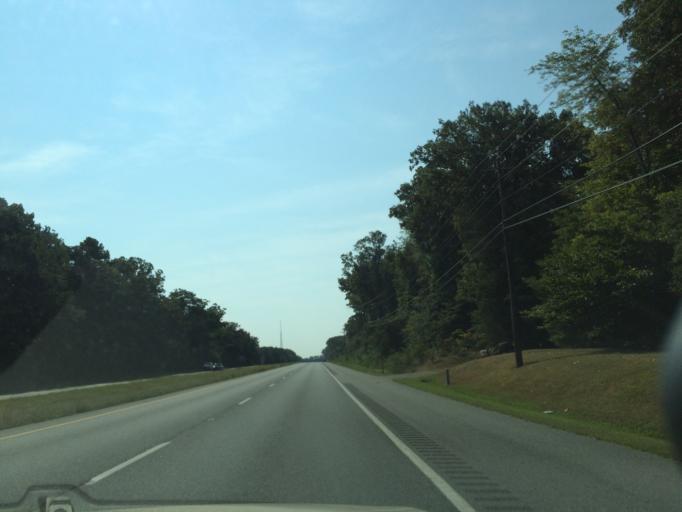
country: US
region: Maryland
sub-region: Charles County
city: La Plata
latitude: 38.4228
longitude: -76.9651
